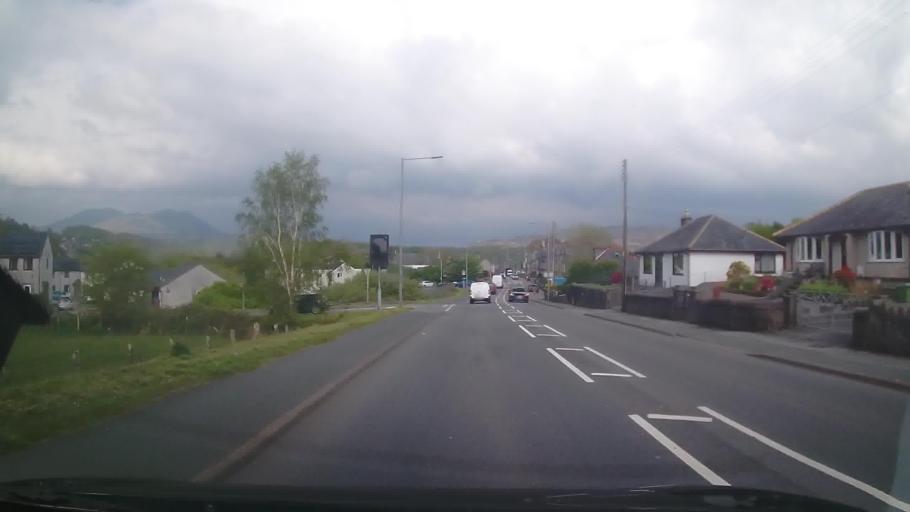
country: GB
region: Wales
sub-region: Gwynedd
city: Penrhyndeudraeth
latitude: 52.9288
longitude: -4.0733
